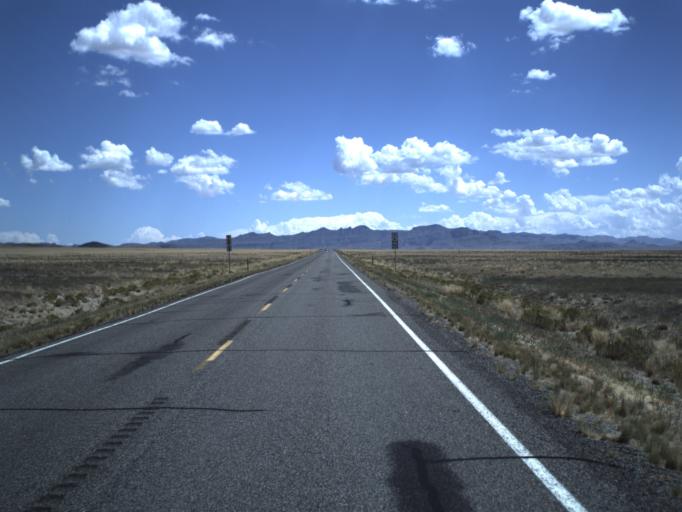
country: US
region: Nevada
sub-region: White Pine County
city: McGill
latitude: 39.0442
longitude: -113.8800
